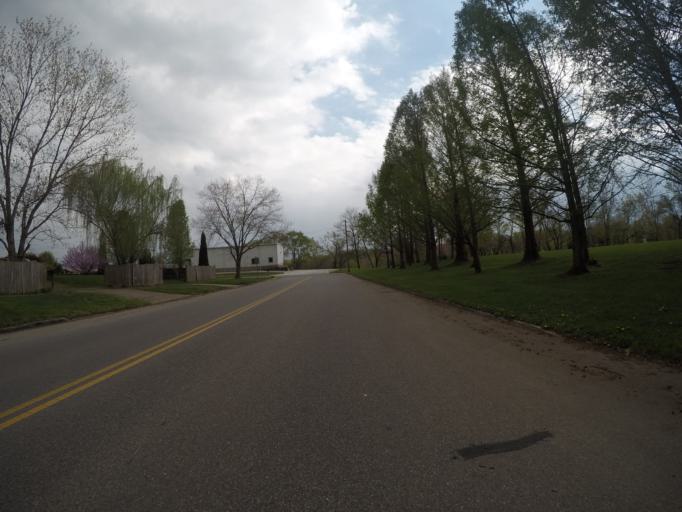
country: US
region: West Virginia
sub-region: Wood County
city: Williamstown
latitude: 39.4111
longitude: -81.4420
